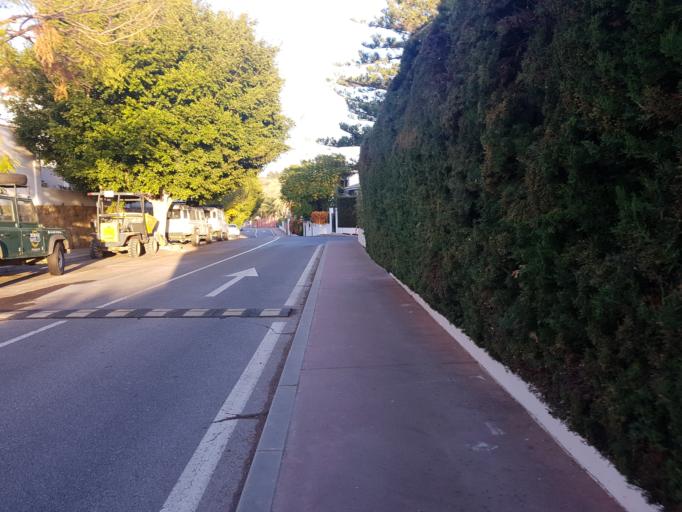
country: ES
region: Andalusia
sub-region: Provincia de Malaga
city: Marbella
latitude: 36.5227
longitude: -4.8904
